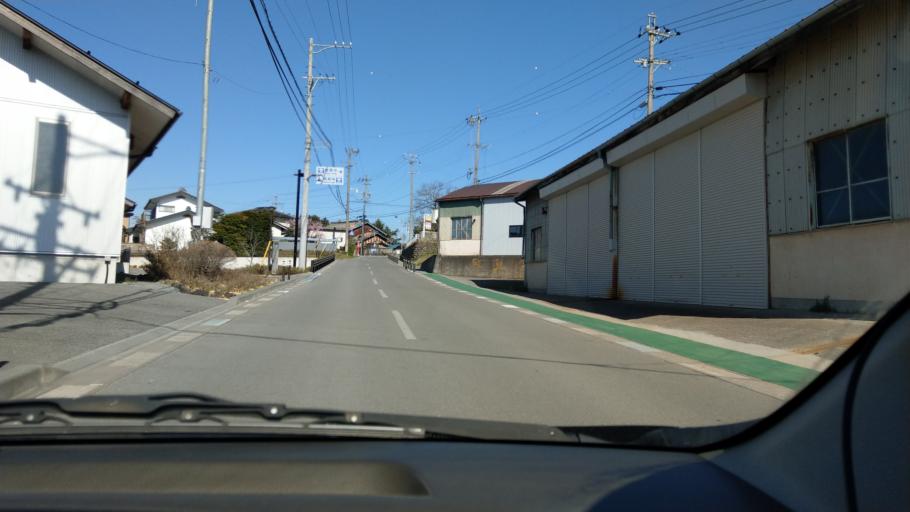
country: JP
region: Nagano
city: Komoro
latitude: 36.3347
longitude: 138.4962
